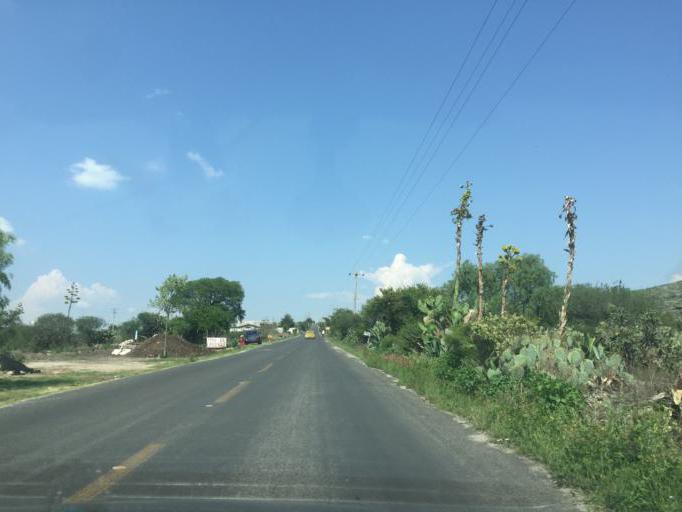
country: MX
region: Hidalgo
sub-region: Cardonal
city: Pozuelos
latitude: 20.6141
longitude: -99.0751
